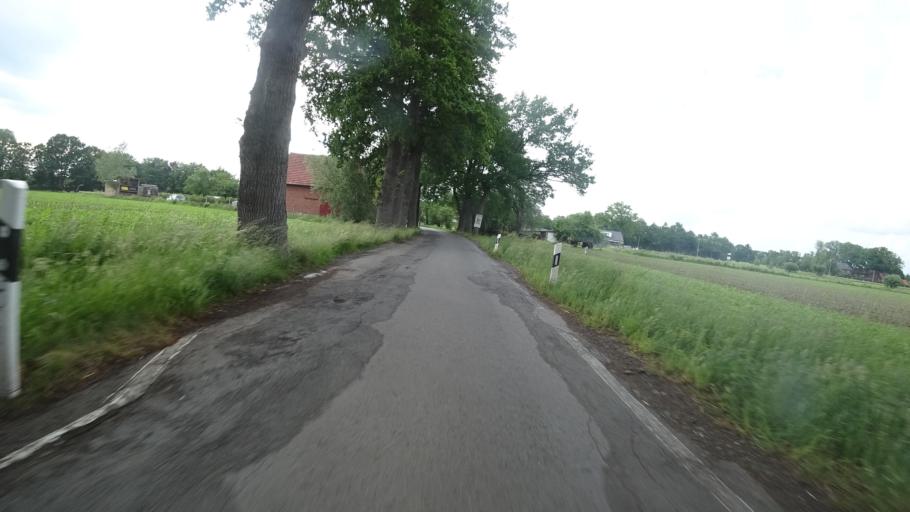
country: DE
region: North Rhine-Westphalia
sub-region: Regierungsbezirk Detmold
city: Guetersloh
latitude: 51.8798
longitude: 8.4112
